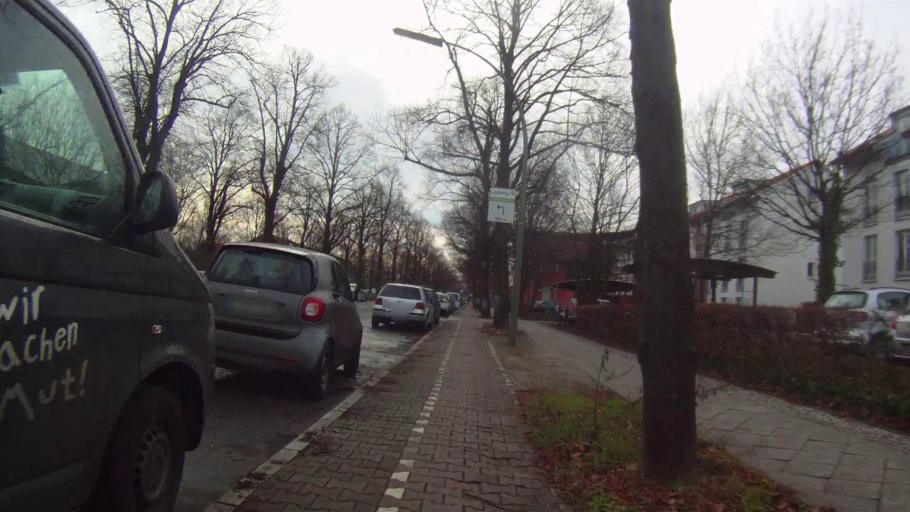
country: DE
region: Berlin
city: Lichtenrade
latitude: 52.3964
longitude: 13.4063
